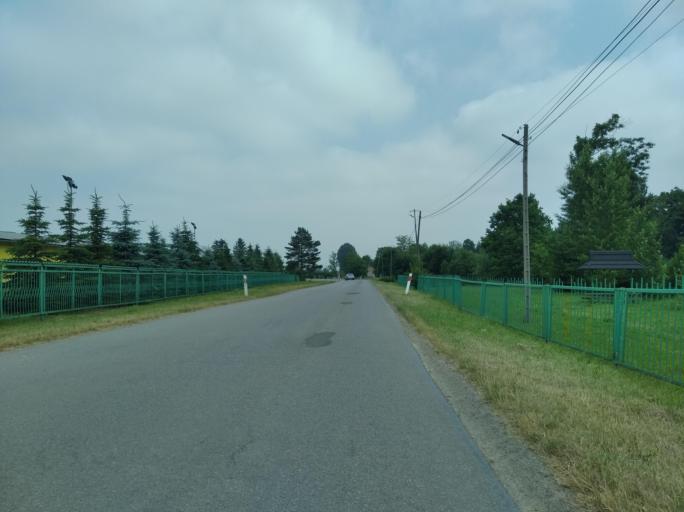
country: PL
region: Subcarpathian Voivodeship
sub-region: Powiat sanocki
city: Besko
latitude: 49.5944
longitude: 21.9609
